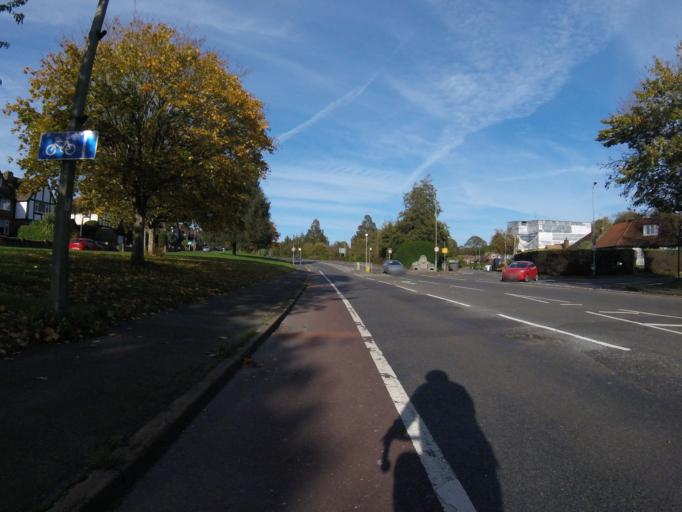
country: GB
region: England
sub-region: Brighton and Hove
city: Hove
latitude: 50.8592
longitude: -0.1523
